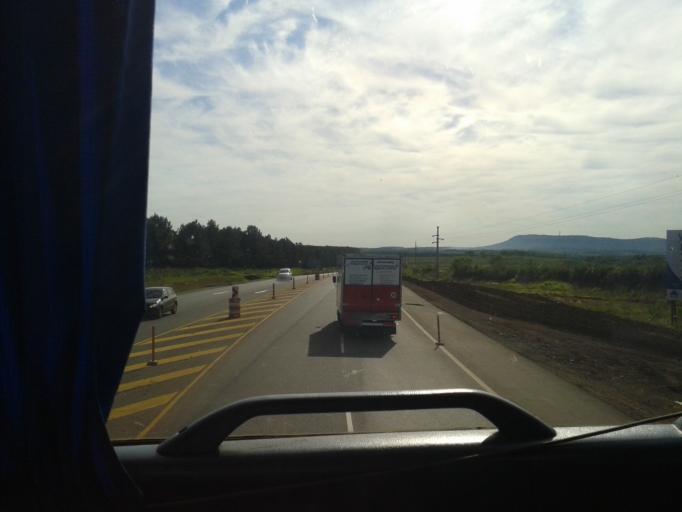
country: AR
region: Misiones
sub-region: Departamento de Candelaria
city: Candelaria
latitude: -27.4614
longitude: -55.6780
